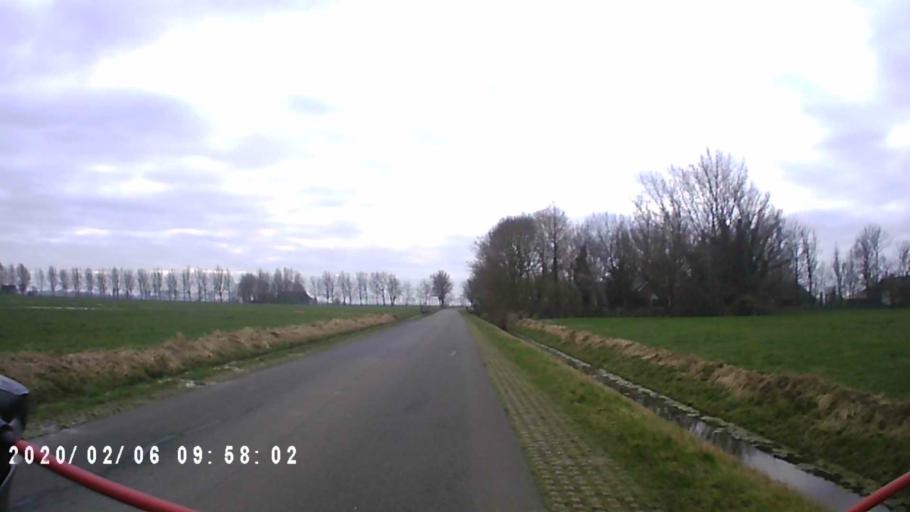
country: NL
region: Groningen
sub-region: Gemeente Zuidhorn
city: Aduard
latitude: 53.2726
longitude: 6.4964
